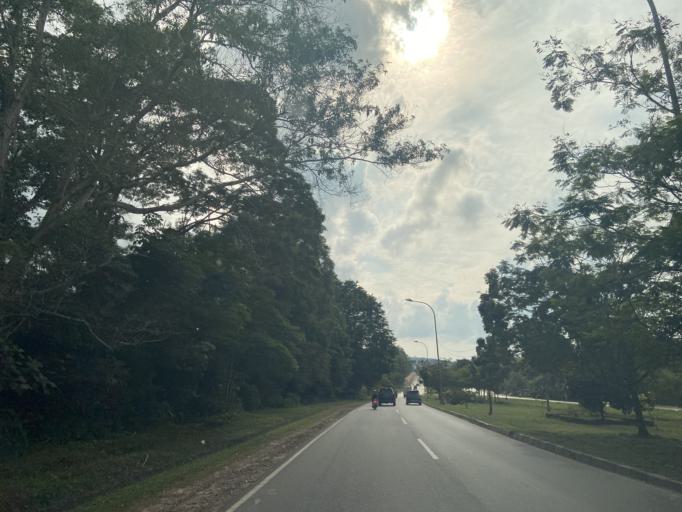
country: SG
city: Singapore
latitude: 1.0988
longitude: 104.0482
